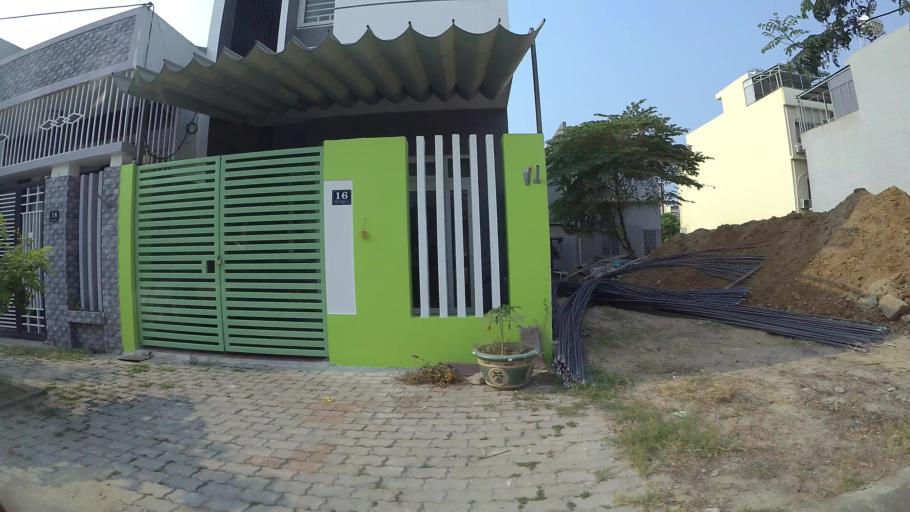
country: VN
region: Da Nang
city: Lien Chieu
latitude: 16.0521
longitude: 108.1677
